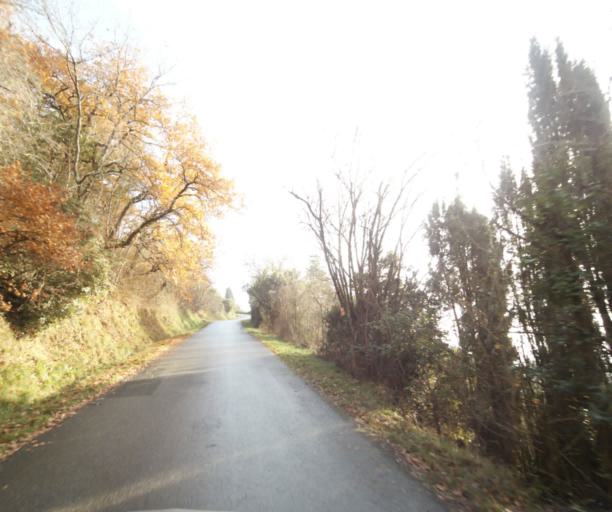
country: FR
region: Midi-Pyrenees
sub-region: Departement de la Haute-Garonne
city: Villemur-sur-Tarn
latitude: 43.8631
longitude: 1.5086
